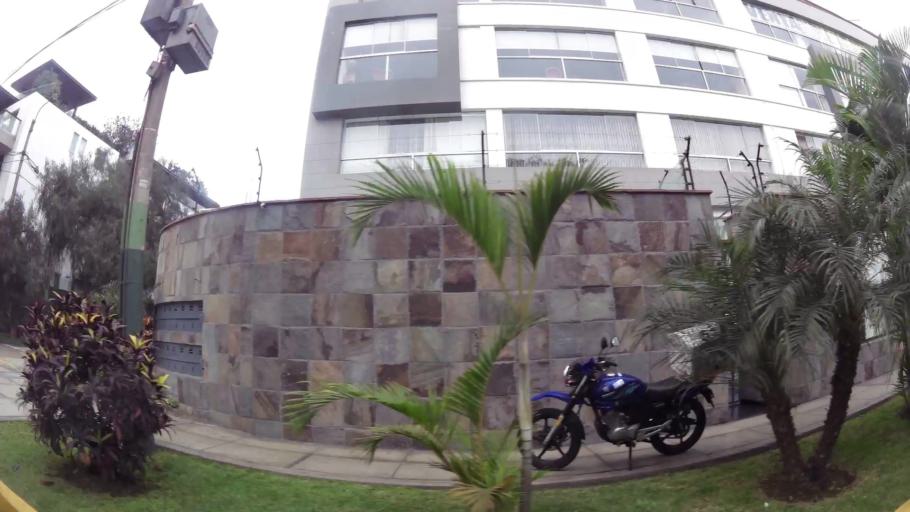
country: PE
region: Lima
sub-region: Lima
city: San Luis
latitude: -12.1064
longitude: -76.9826
